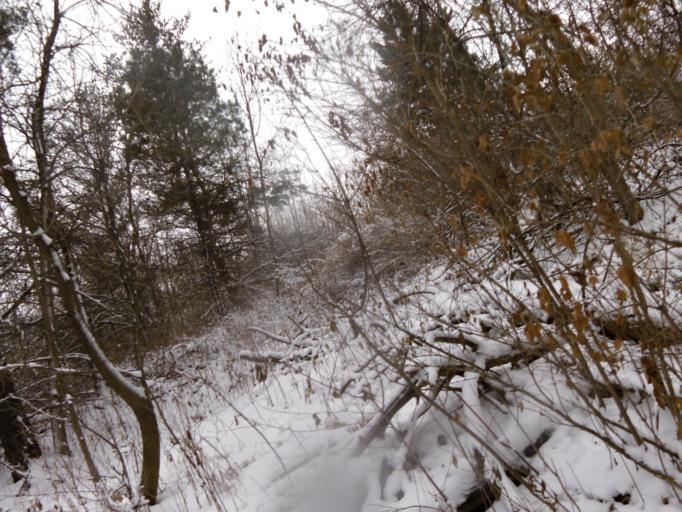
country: US
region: Minnesota
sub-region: Dakota County
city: Inver Grove Heights
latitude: 44.8575
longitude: -93.0715
